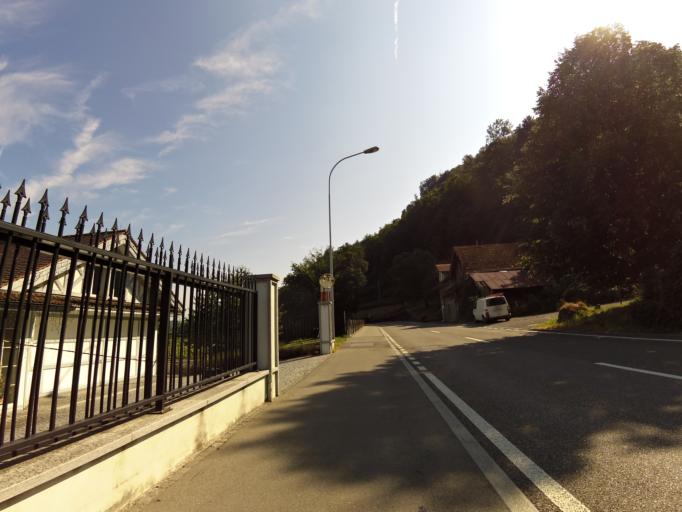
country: CH
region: Zug
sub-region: Zug
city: Walchwil
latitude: 47.1305
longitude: 8.5006
